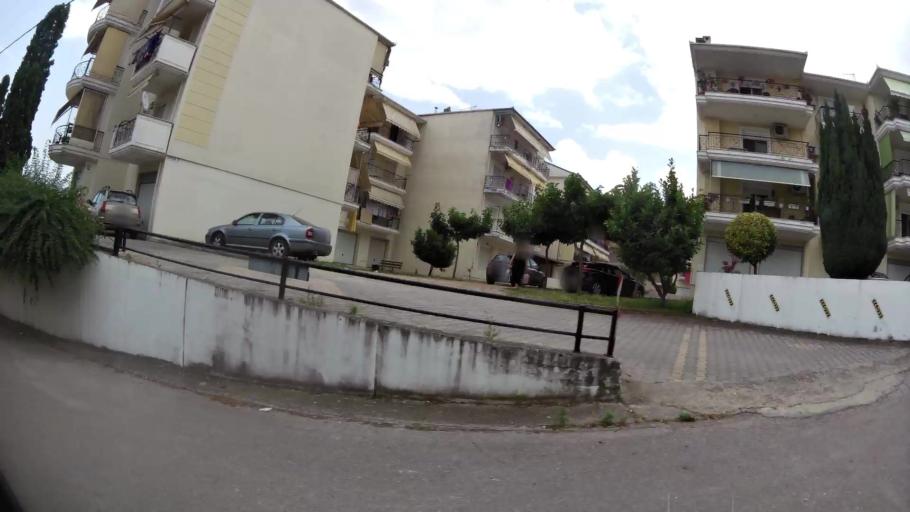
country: GR
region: Central Macedonia
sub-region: Nomos Imathias
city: Veroia
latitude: 40.5229
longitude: 22.2098
